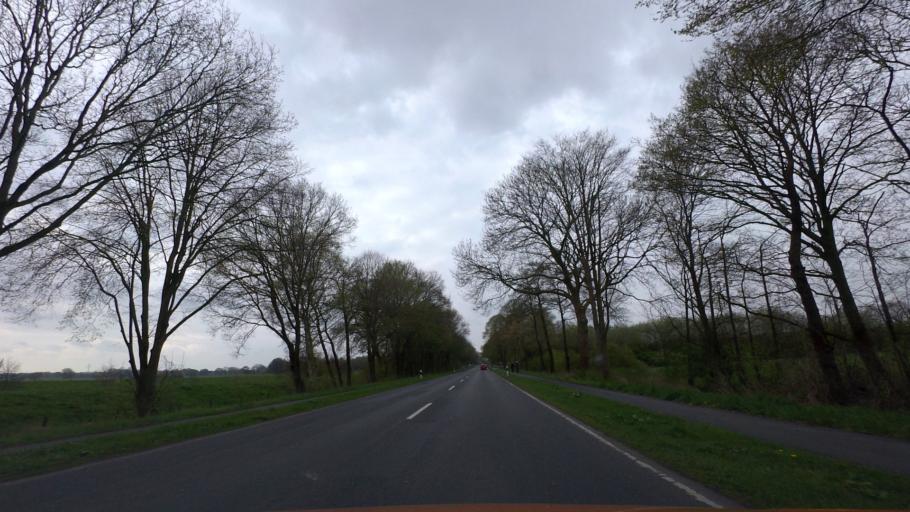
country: DE
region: Lower Saxony
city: Wardenburg
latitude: 53.0985
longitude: 8.1968
